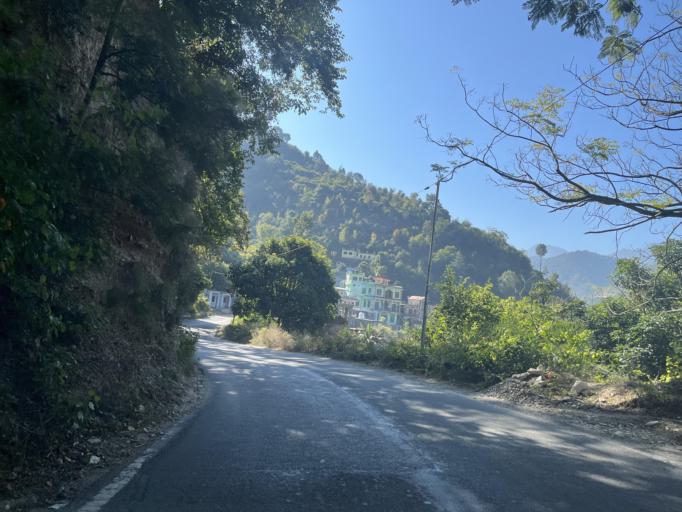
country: IN
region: Uttarakhand
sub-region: Almora
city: Ranikhet
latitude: 29.5223
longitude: 79.4820
